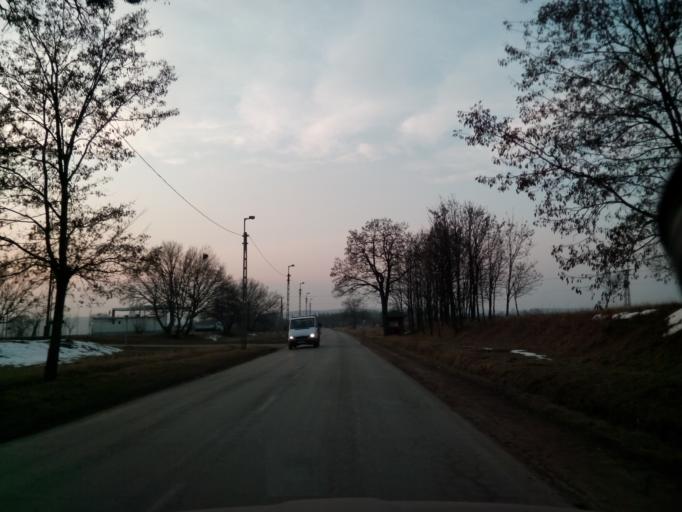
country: HU
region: Borsod-Abauj-Zemplen
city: Gonc
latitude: 48.4769
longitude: 21.2650
